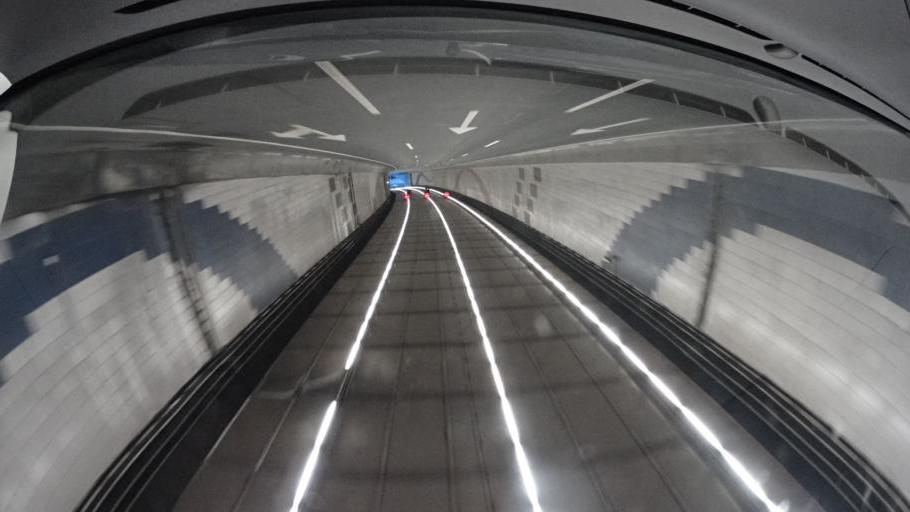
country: ES
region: Basque Country
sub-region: Bizkaia
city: Bilbao
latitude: 43.2714
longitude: -2.9560
